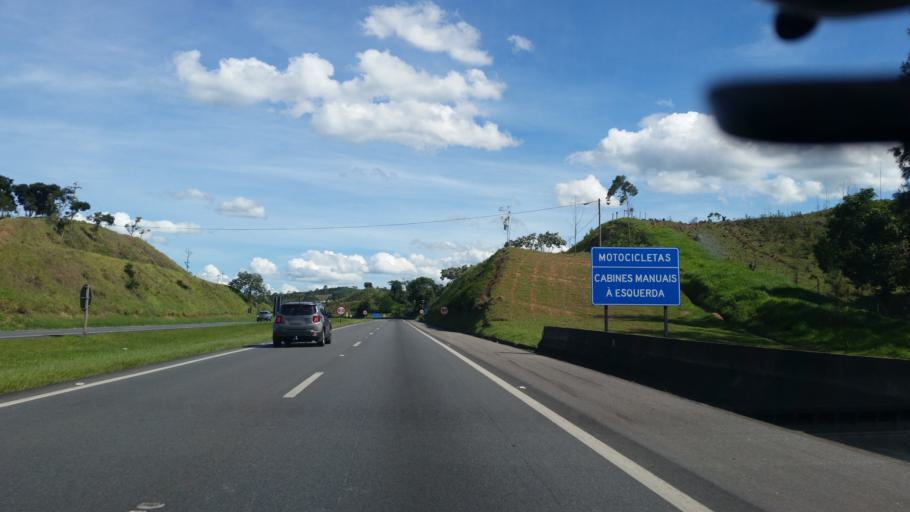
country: BR
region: Sao Paulo
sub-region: Santa Isabel
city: Santa Isabel
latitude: -23.1950
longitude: -46.1858
